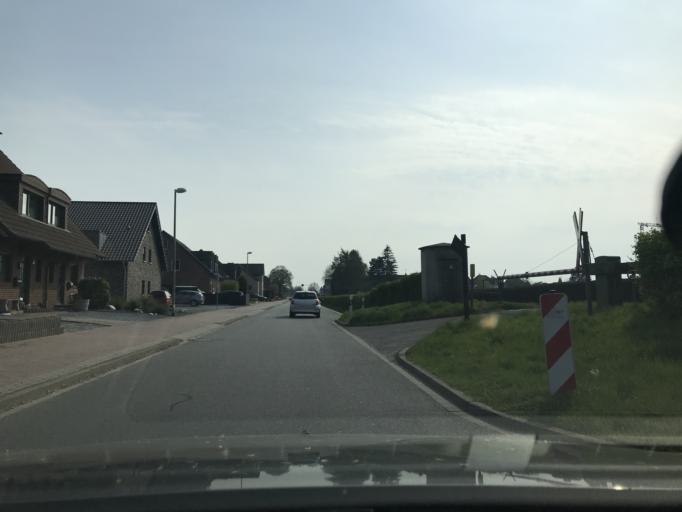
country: DE
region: North Rhine-Westphalia
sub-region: Regierungsbezirk Dusseldorf
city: Goch
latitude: 51.7201
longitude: 6.1659
